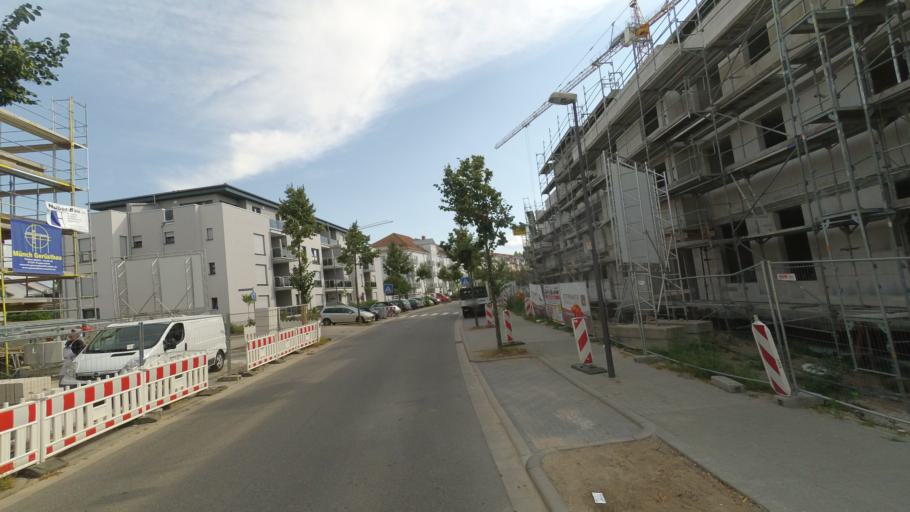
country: DE
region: Rheinland-Pfalz
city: Frankenthal
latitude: 49.5028
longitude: 8.3818
